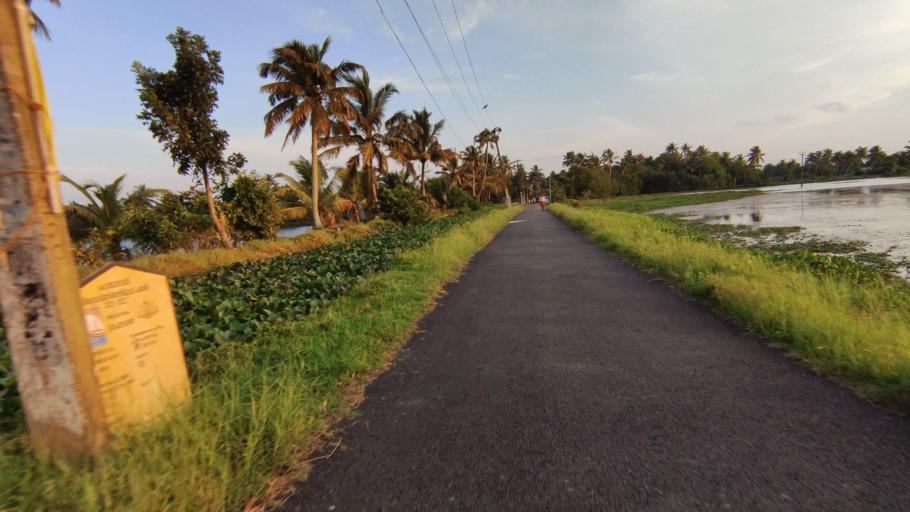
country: IN
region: Kerala
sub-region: Kottayam
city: Kottayam
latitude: 9.5729
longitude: 76.4351
